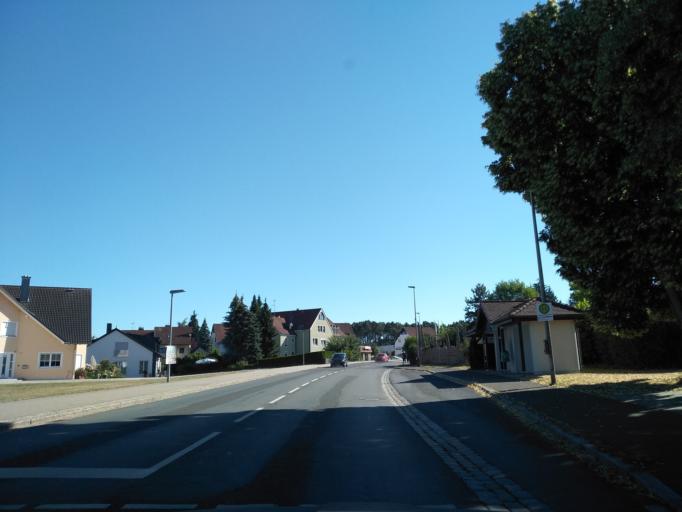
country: DE
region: Bavaria
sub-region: Regierungsbezirk Mittelfranken
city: Rottenbach
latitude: 49.6647
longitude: 10.9229
